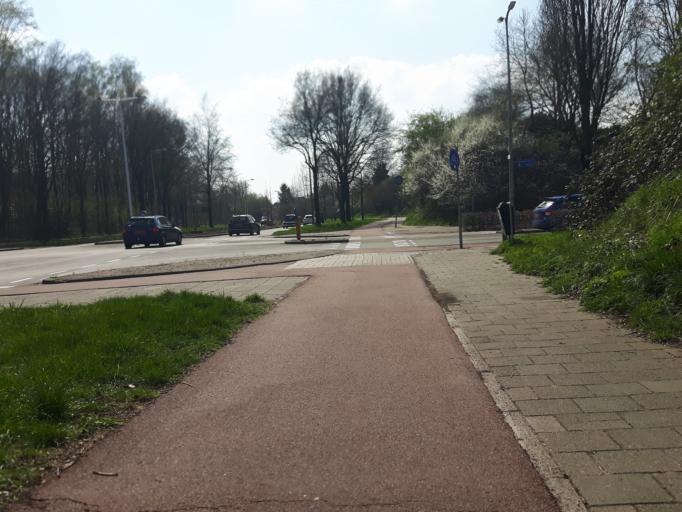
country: NL
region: Overijssel
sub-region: Gemeente Enschede
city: Enschede
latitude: 52.1964
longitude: 6.8601
